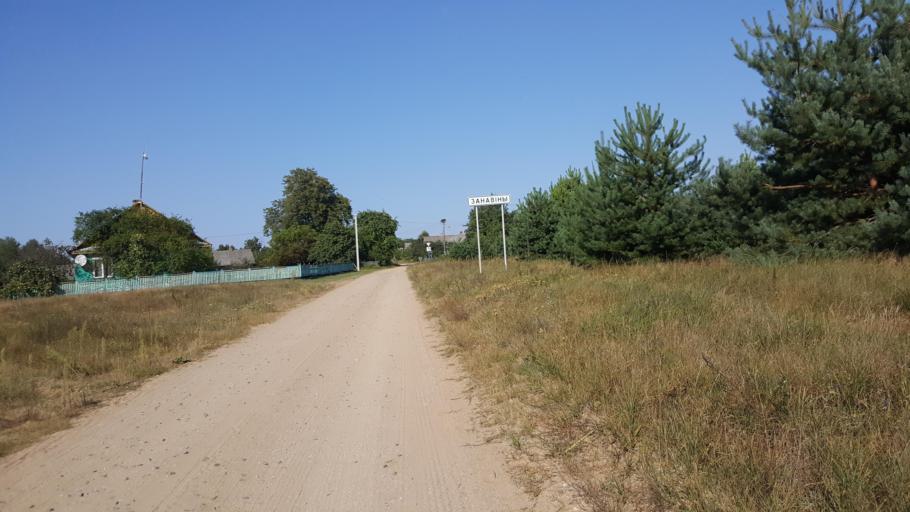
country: BY
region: Brest
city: Kamyanyuki
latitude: 52.5685
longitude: 23.6269
